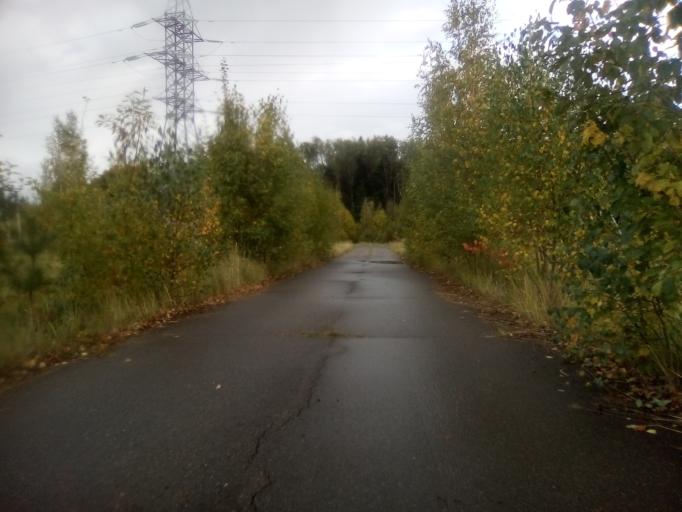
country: RU
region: Moskovskaya
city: Aprelevka
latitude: 55.5658
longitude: 37.0706
